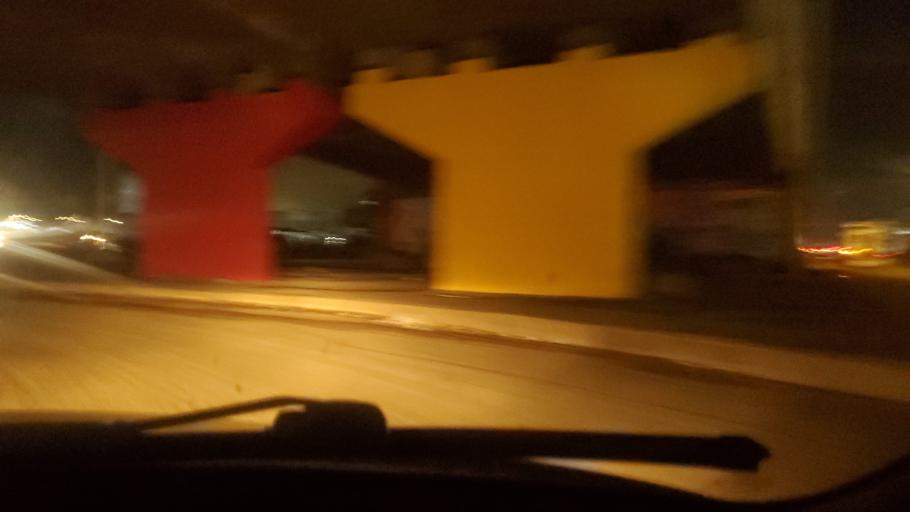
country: SN
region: Dakar
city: Pikine
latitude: 14.7456
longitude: -17.3776
